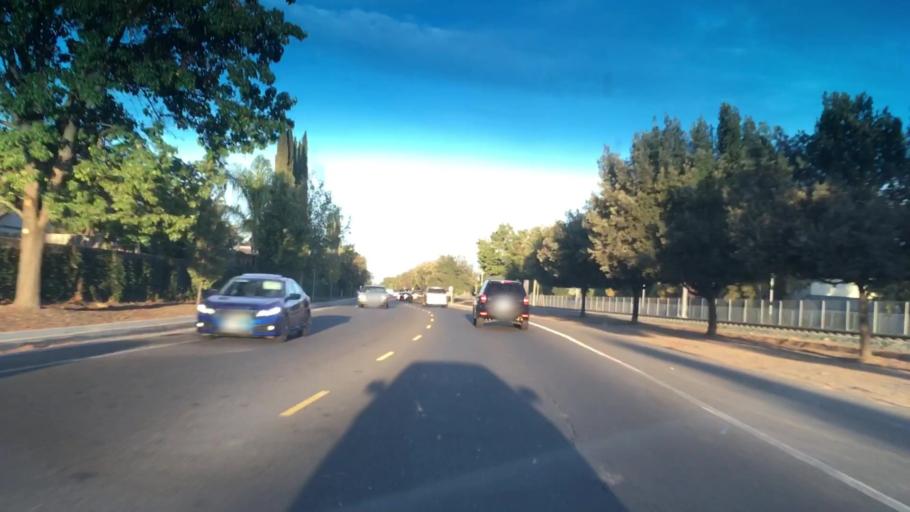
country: US
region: California
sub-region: Sacramento County
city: Laguna
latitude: 38.4589
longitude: -121.4311
